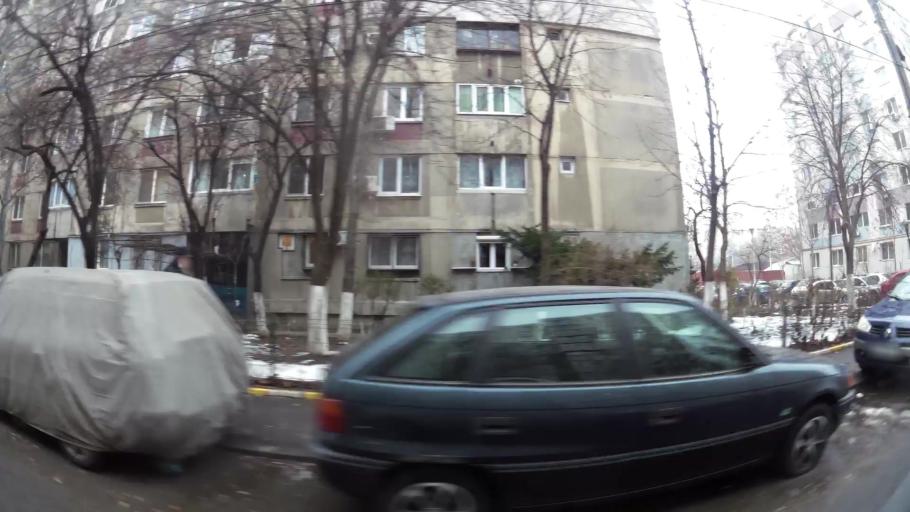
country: RO
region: Ilfov
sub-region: Comuna Chiajna
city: Rosu
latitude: 44.4557
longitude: 26.0465
